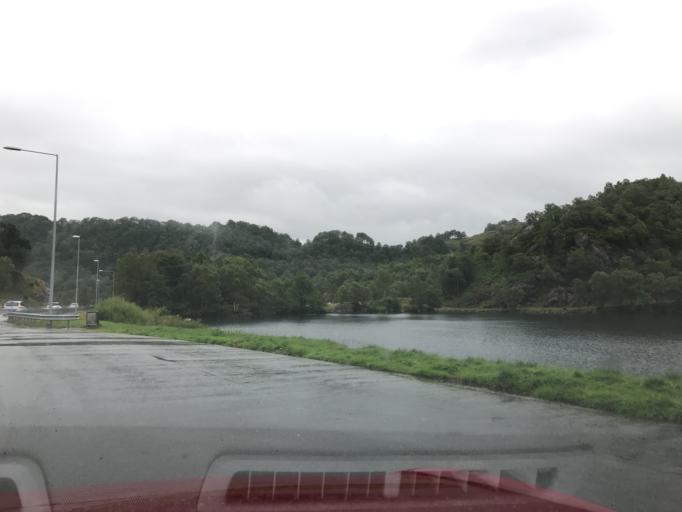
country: NO
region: Rogaland
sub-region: Bjerkreim
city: Vikesa
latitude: 58.5528
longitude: 6.0700
